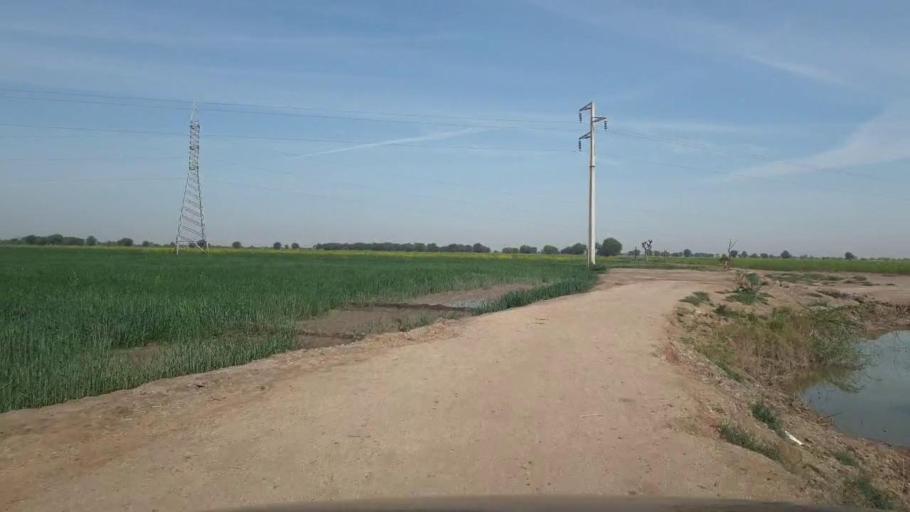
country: PK
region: Sindh
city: Umarkot
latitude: 25.3645
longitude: 69.6089
